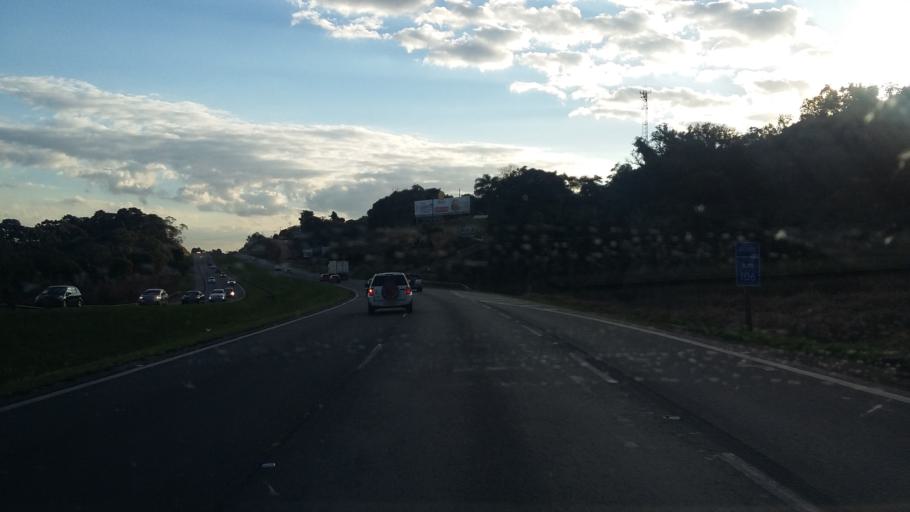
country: BR
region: Parana
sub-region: Campo Largo
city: Campo Largo
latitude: -25.4307
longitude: -49.4225
